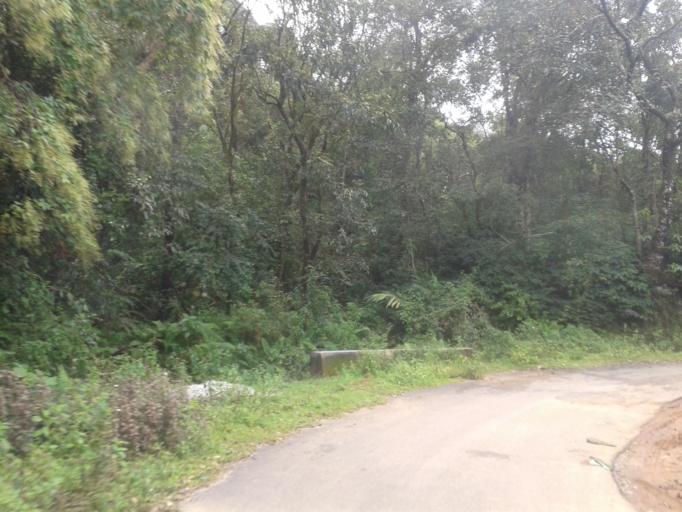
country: IN
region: Karnataka
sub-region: Chikmagalur
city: Mudigere
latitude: 12.9897
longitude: 75.6201
